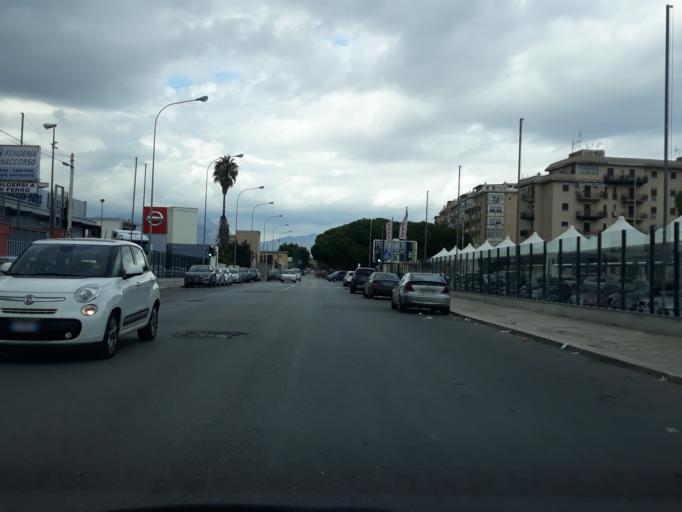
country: IT
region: Sicily
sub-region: Palermo
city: Ciaculli
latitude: 38.0947
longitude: 13.4005
